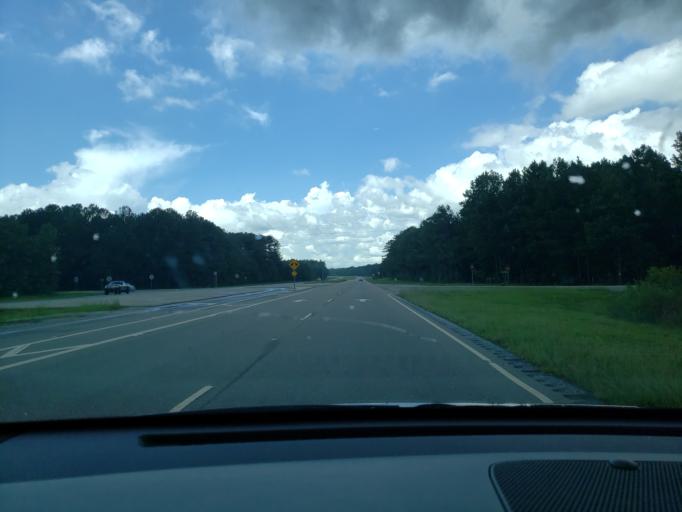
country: US
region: North Carolina
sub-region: Bladen County
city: Elizabethtown
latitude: 34.6251
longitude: -78.6505
